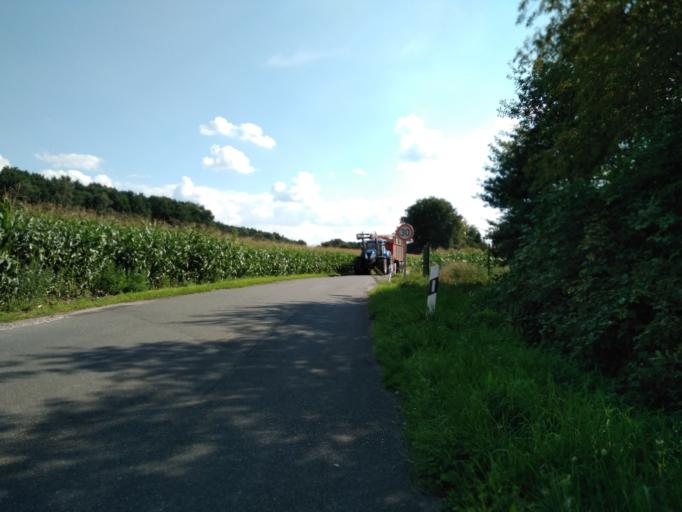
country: DE
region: North Rhine-Westphalia
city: Dorsten
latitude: 51.7242
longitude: 6.9712
